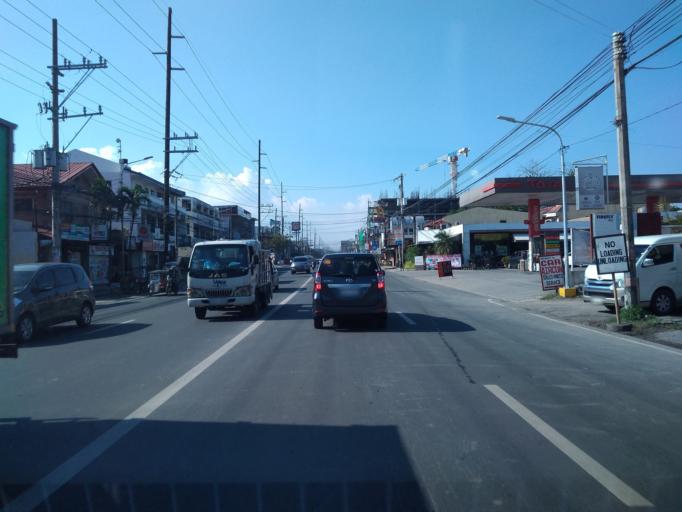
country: PH
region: Calabarzon
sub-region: Province of Laguna
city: Calamba
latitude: 14.1921
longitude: 121.1667
